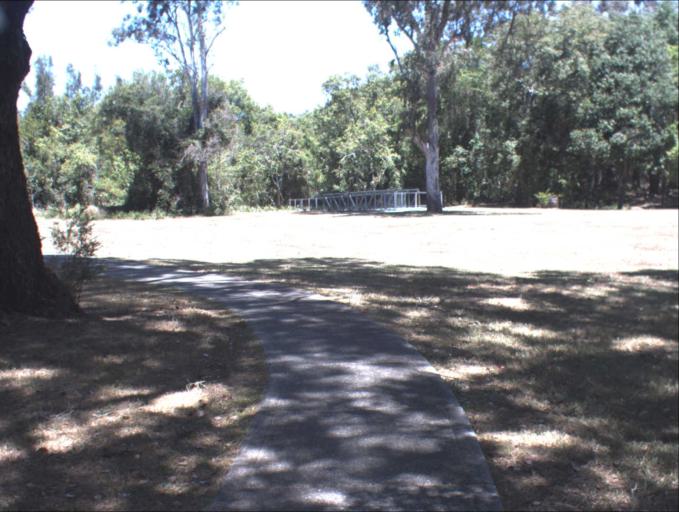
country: AU
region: Queensland
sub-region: Gold Coast
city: Yatala
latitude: -27.7149
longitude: 153.2120
